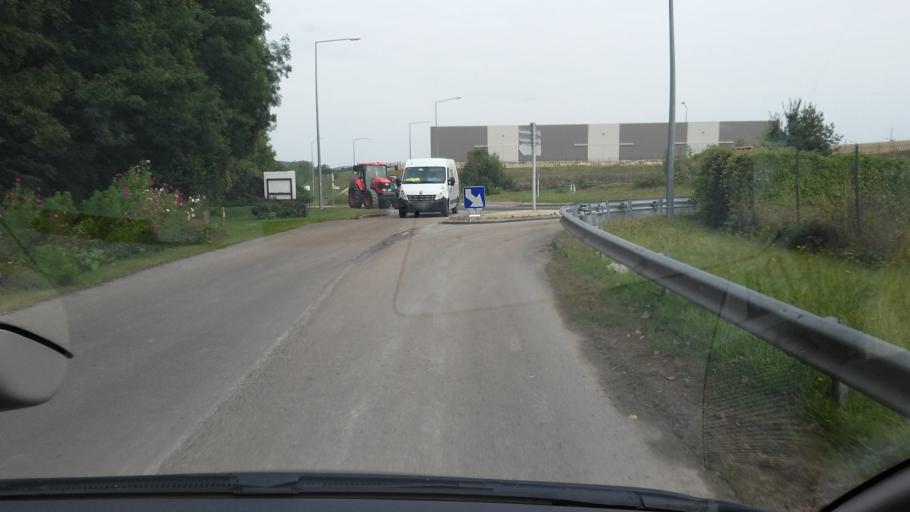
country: FR
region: Champagne-Ardenne
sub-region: Departement de la Marne
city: Mareuil-sur-Ay
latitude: 49.0749
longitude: 4.0591
